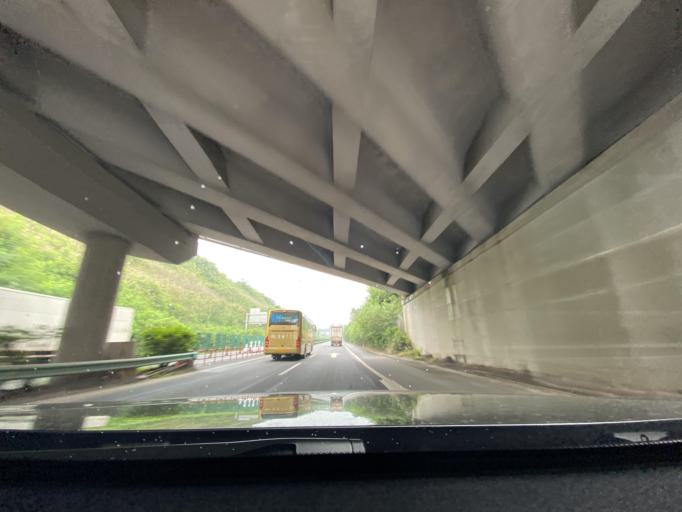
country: CN
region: Sichuan
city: Longquan
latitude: 30.2998
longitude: 104.1216
